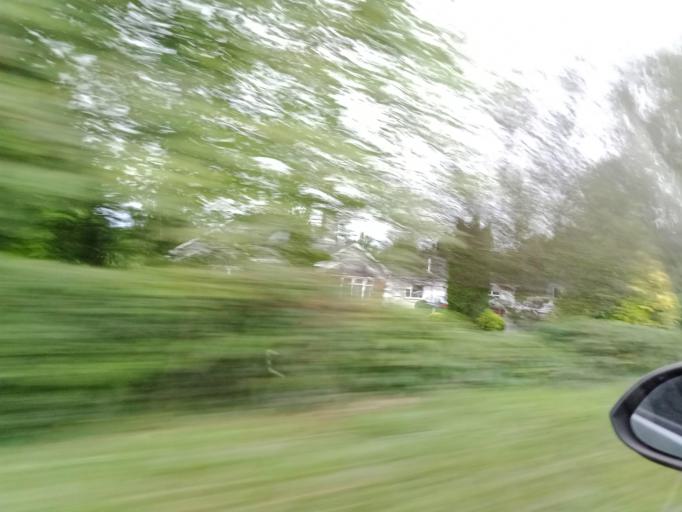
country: IE
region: Leinster
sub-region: Laois
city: Mountmellick
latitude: 53.1171
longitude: -7.3626
